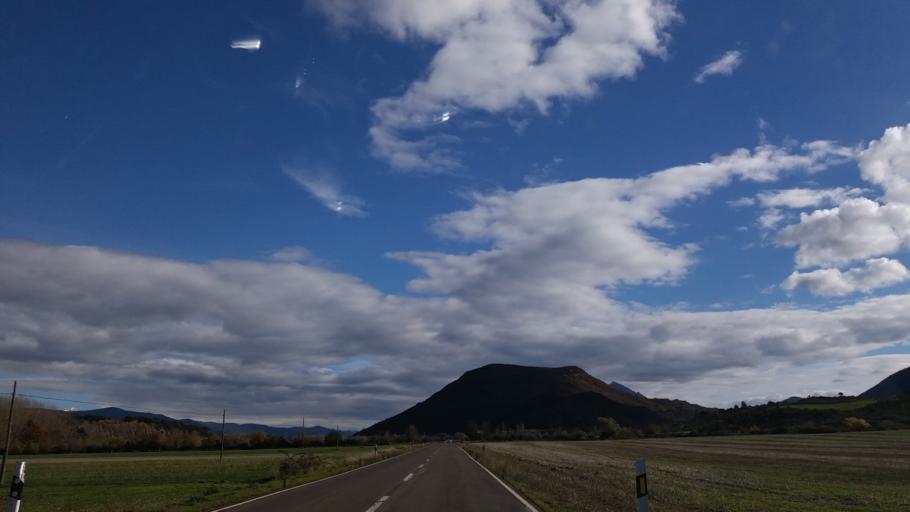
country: ES
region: Aragon
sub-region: Provincia de Huesca
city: Santa Cruz de la Seros
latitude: 42.5564
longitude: -0.6949
